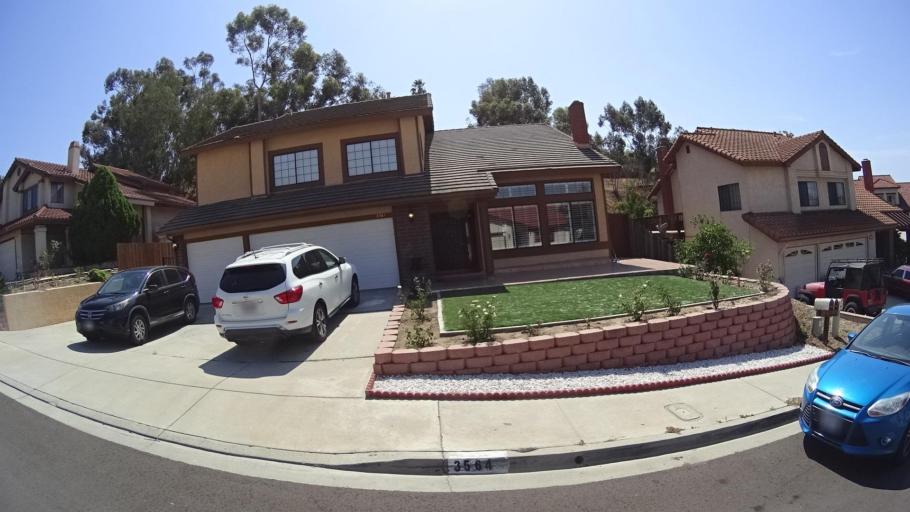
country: US
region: California
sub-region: San Diego County
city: Spring Valley
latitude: 32.7430
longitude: -116.9923
